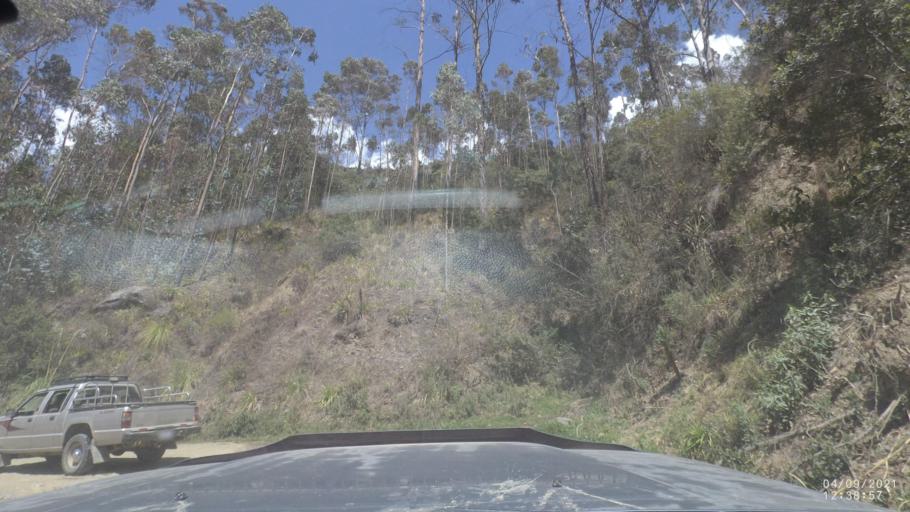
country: BO
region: Cochabamba
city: Colchani
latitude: -17.2291
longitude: -66.5004
